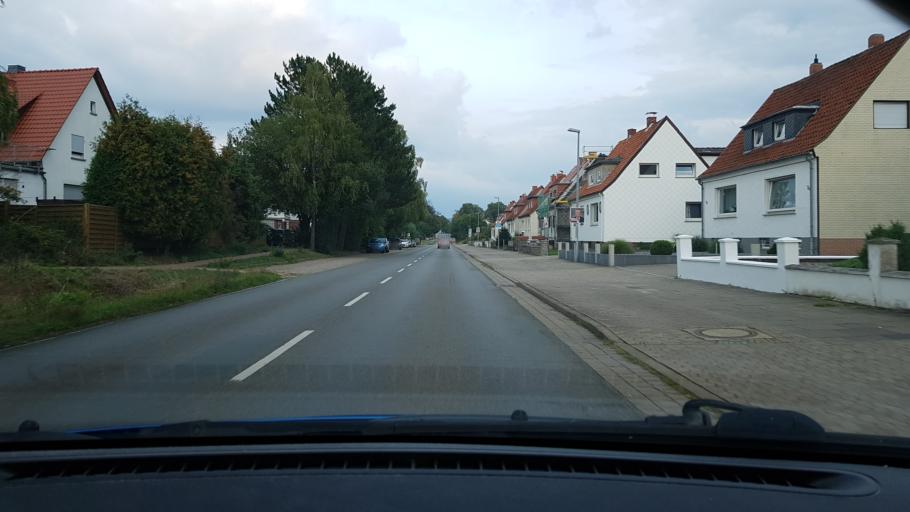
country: DE
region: Lower Saxony
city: Bad Munder am Deister
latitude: 52.1970
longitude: 9.4503
